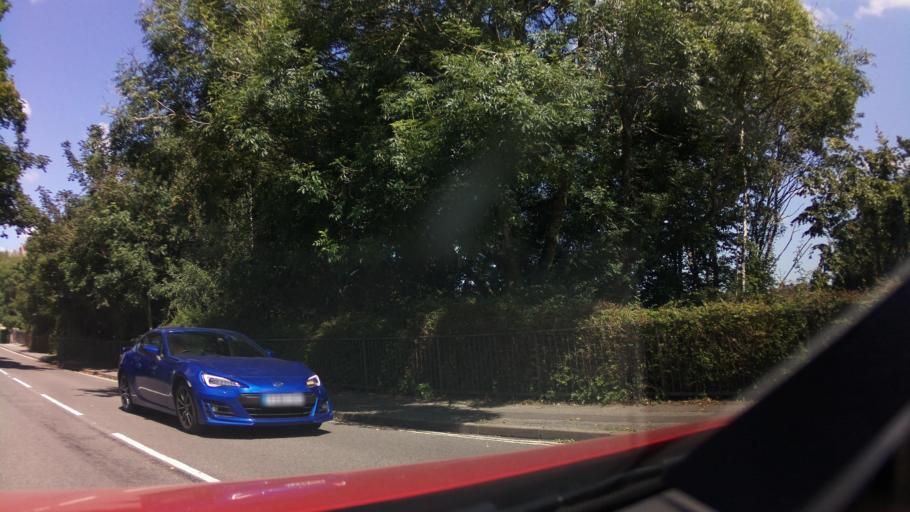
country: GB
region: England
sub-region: Derbyshire
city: Ashbourne
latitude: 53.0140
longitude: -1.7355
